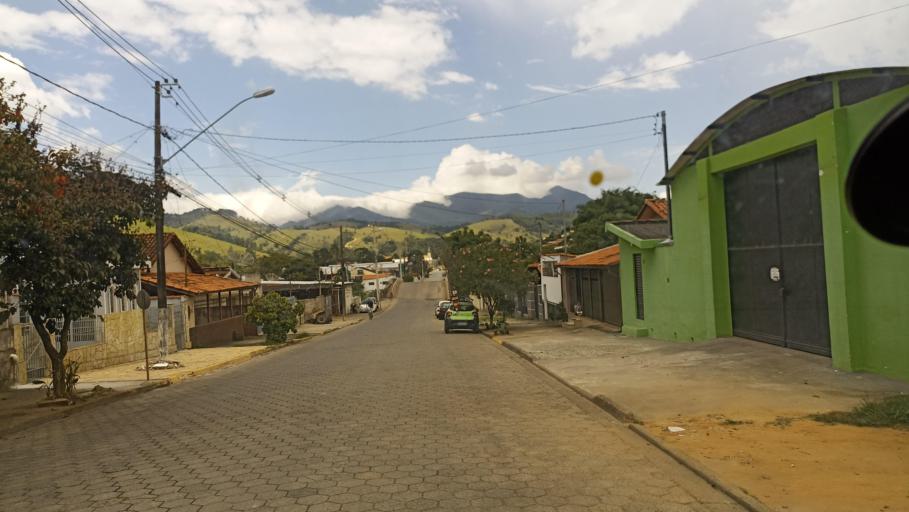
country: BR
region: Minas Gerais
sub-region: Passa Quatro
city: Passa Quatro
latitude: -22.3788
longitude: -44.9672
